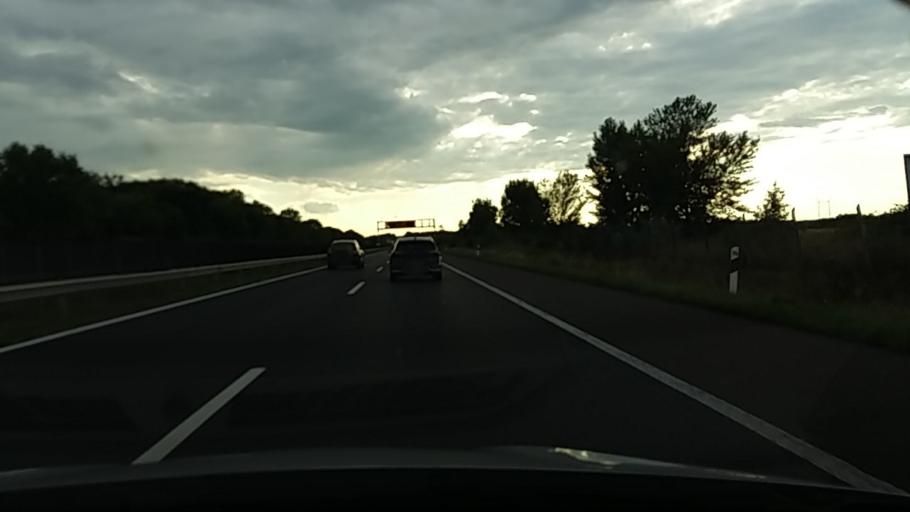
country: HU
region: Heves
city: Gyongyoshalasz
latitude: 47.7271
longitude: 19.8838
